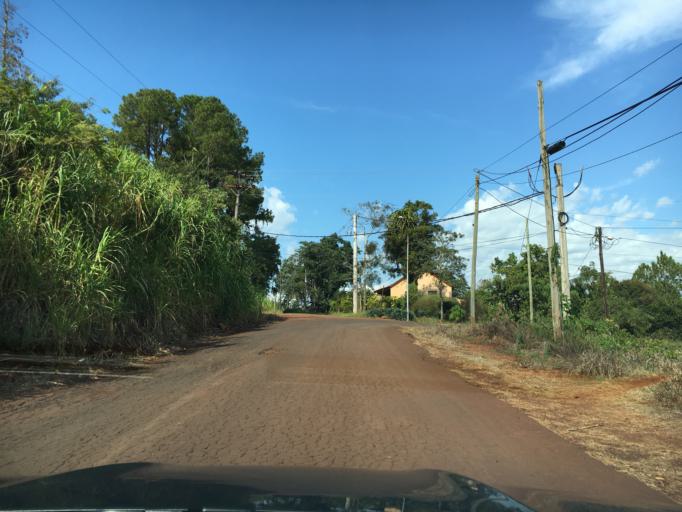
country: AR
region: Misiones
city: Puerto Rico
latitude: -26.8061
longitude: -55.0073
